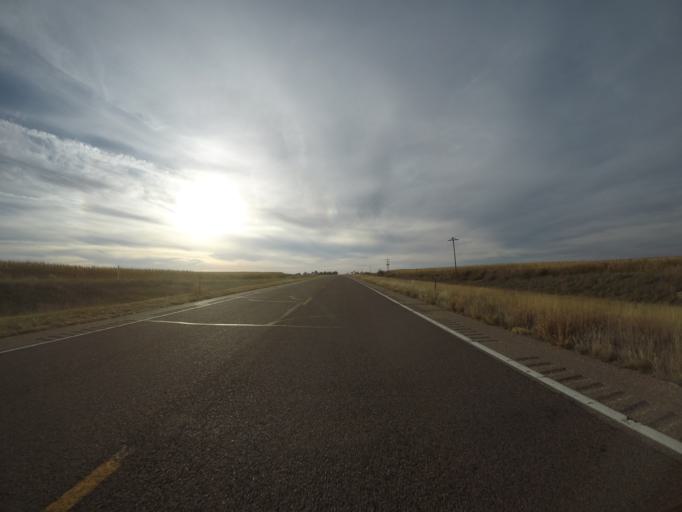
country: US
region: Colorado
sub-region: Kit Carson County
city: Burlington
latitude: 39.6580
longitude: -102.5210
